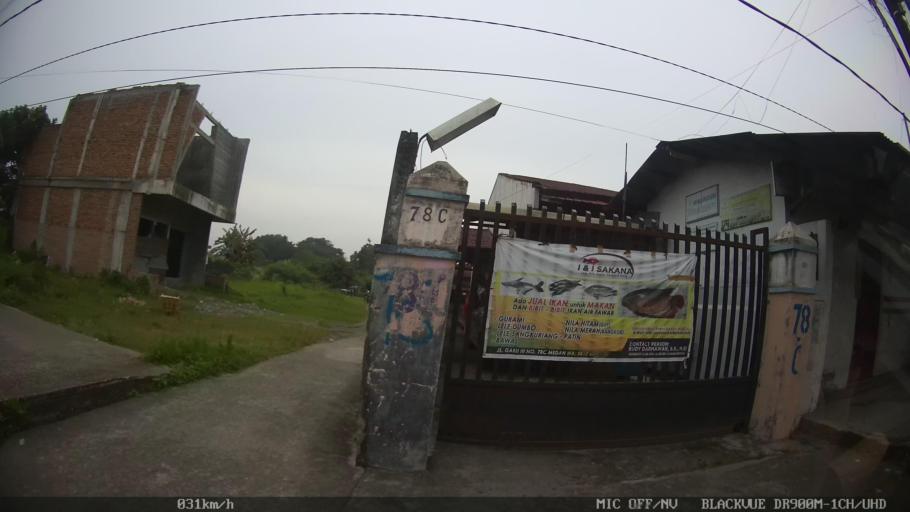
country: ID
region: North Sumatra
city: Deli Tua
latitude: 3.5434
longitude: 98.7045
